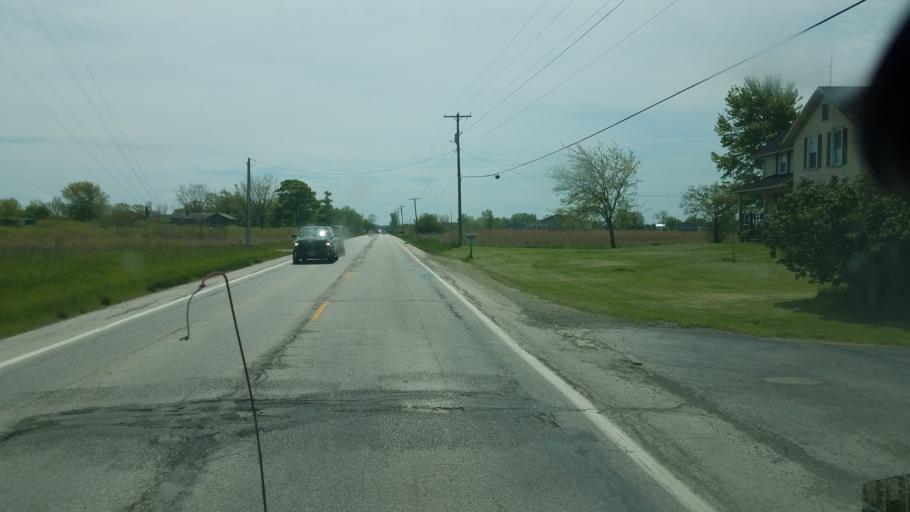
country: US
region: Ohio
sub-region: Ottawa County
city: Oak Harbor
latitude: 41.5774
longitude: -83.0895
